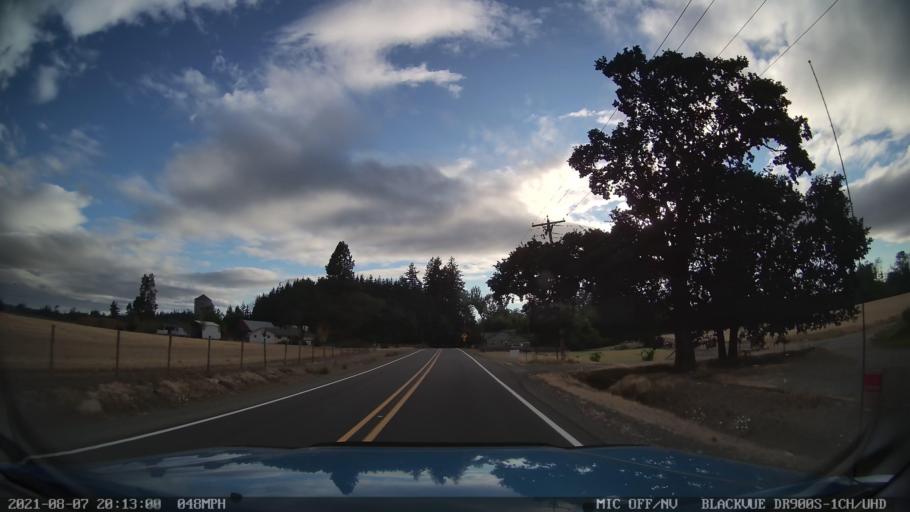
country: US
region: Oregon
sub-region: Marion County
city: Hayesville
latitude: 44.9568
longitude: -122.9174
